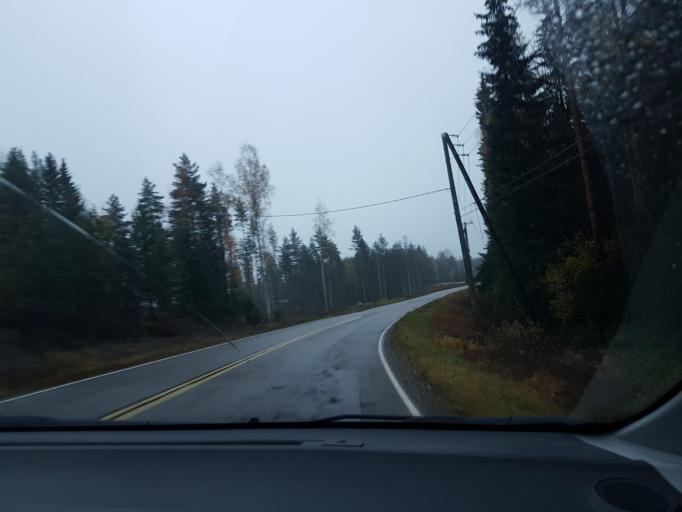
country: FI
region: Uusimaa
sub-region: Helsinki
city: Jaervenpaeae
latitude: 60.5815
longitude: 25.1661
